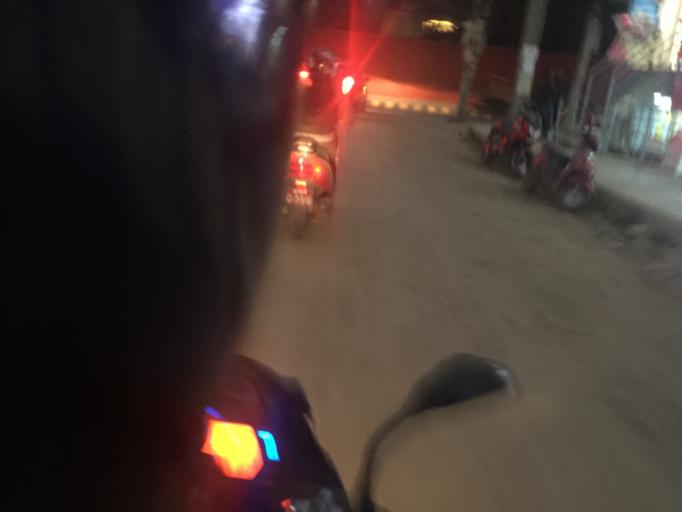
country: NP
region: Central Region
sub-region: Bagmati Zone
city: Patan
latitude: 27.6792
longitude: 85.3080
